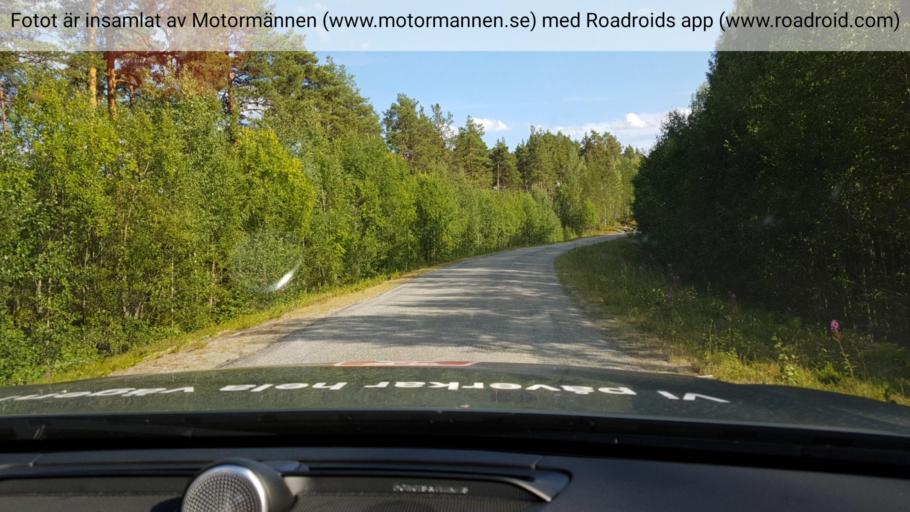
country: SE
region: Vaesterbotten
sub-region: Dorotea Kommun
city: Dorotea
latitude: 63.9194
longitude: 16.2629
